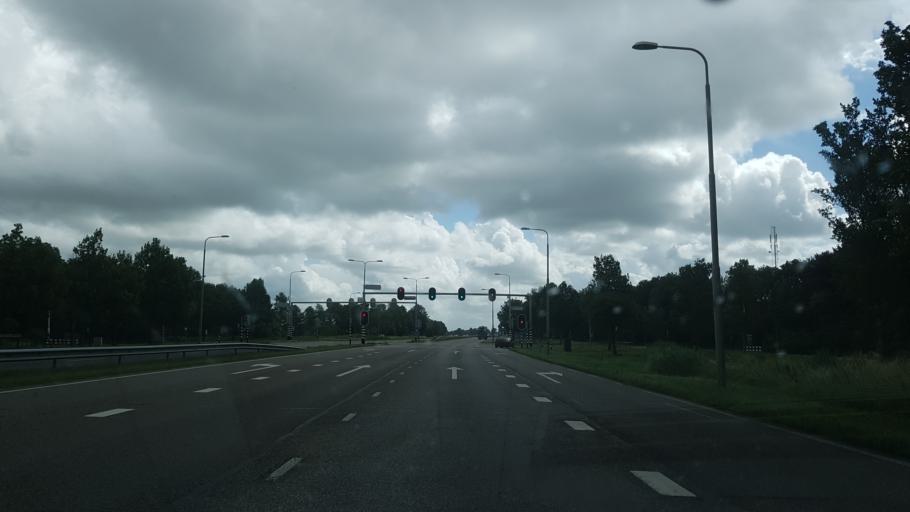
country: NL
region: Friesland
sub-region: Gemeente Leeuwarden
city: Camminghaburen
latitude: 53.2175
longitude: 5.8650
